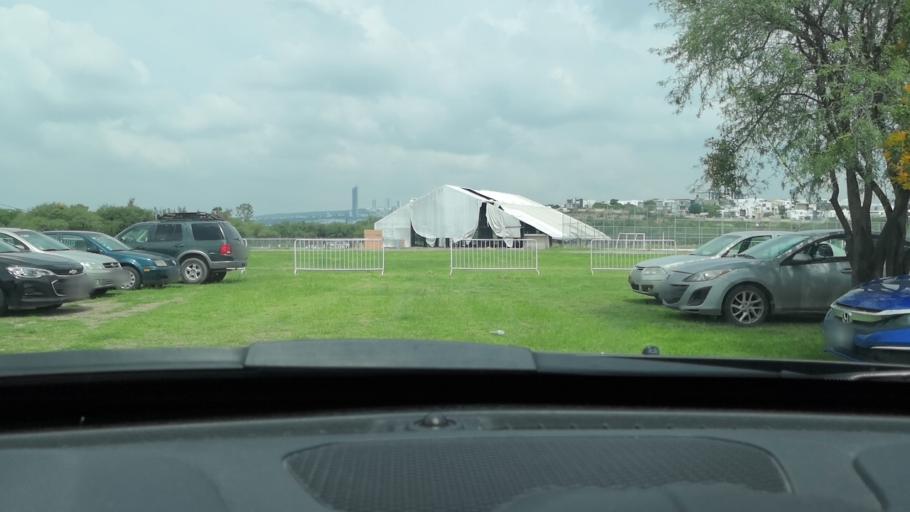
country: MX
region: Guanajuato
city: Leon
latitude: 21.1893
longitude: -101.6836
